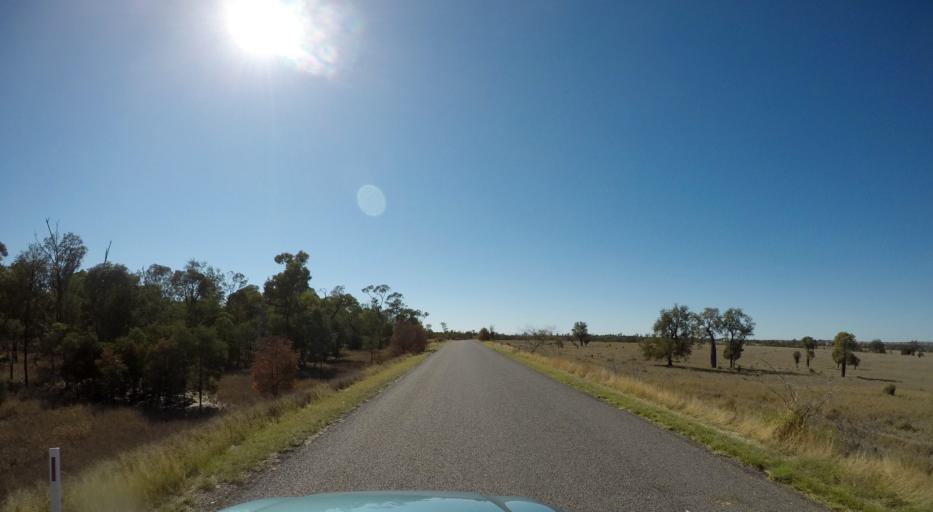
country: AU
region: Queensland
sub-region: Banana
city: Taroom
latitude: -25.7885
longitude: 149.6898
